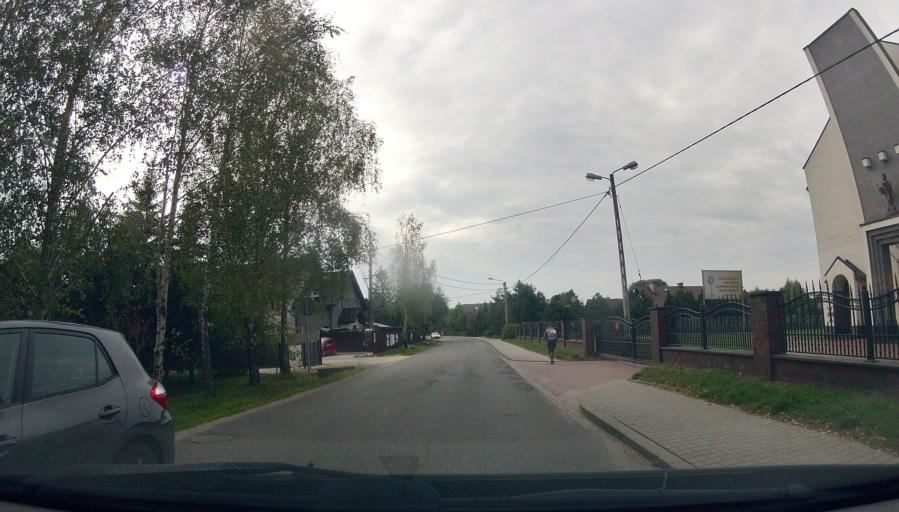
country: PL
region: Lesser Poland Voivodeship
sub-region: Powiat wielicki
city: Wieliczka
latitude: 49.9879
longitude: 20.0324
